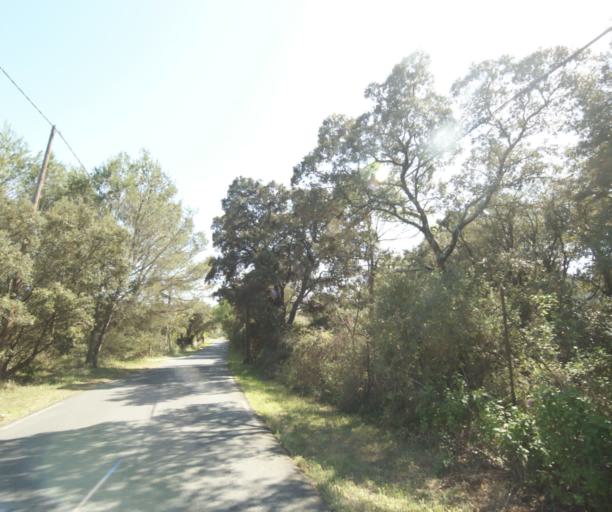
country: FR
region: Languedoc-Roussillon
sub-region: Departement de l'Herault
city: Sussargues
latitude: 43.6956
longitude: 3.9984
